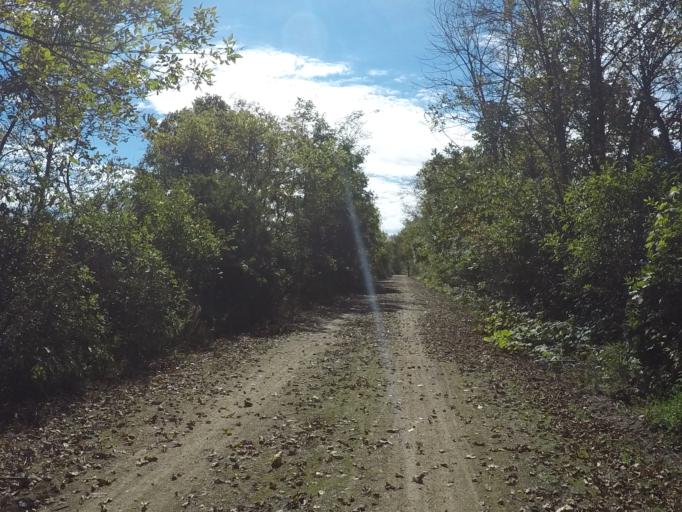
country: US
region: Wisconsin
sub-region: Richland County
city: Richland Center
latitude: 43.2693
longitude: -90.3076
